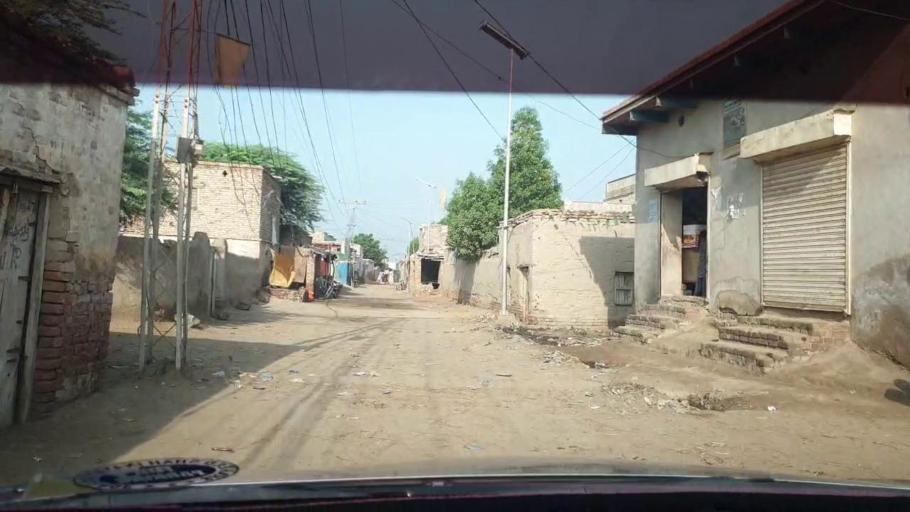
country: PK
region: Sindh
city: Goth Garelo
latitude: 27.4843
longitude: 68.0381
